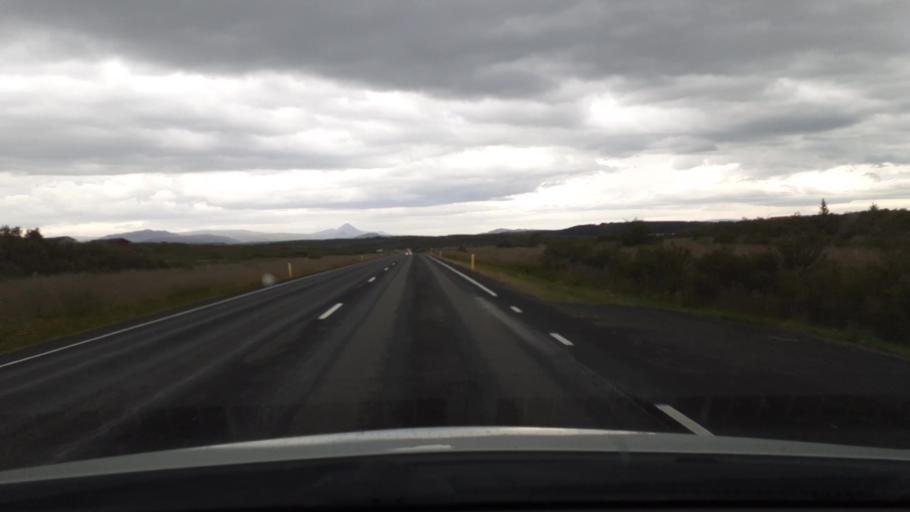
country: IS
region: West
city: Borgarnes
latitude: 64.6506
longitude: -21.7414
